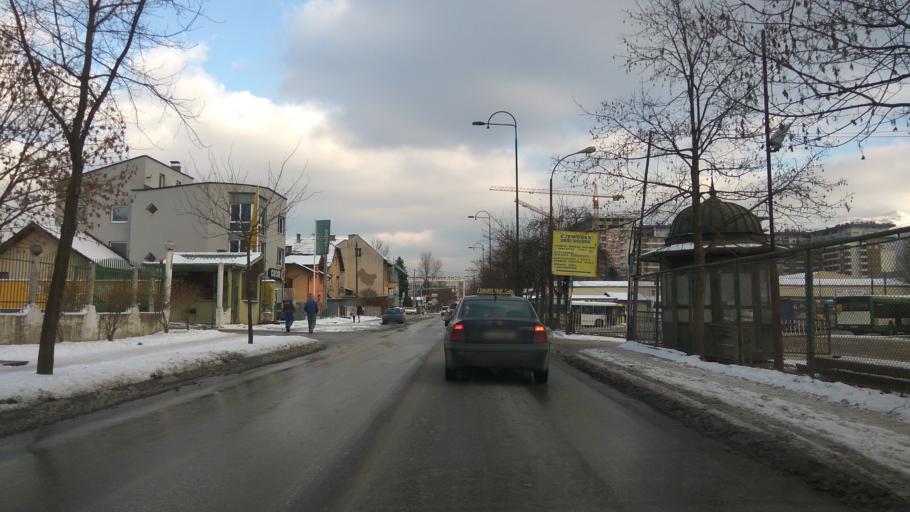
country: BA
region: Federation of Bosnia and Herzegovina
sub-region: Kanton Sarajevo
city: Sarajevo
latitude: 43.8502
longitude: 18.3583
